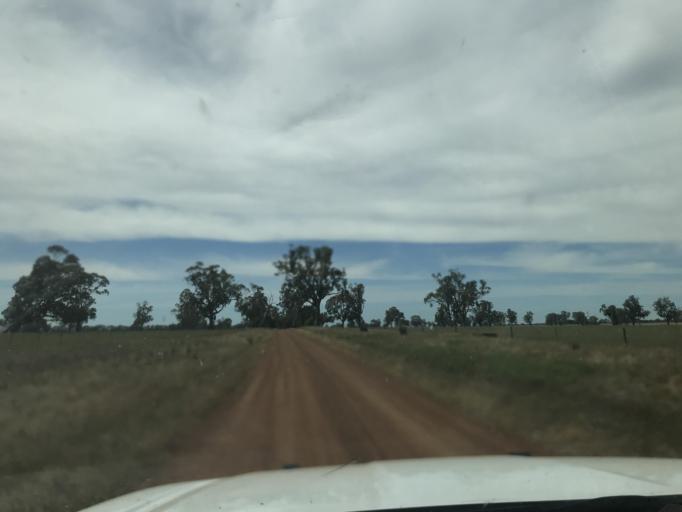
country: AU
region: South Australia
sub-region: Naracoorte and Lucindale
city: Naracoorte
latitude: -37.0054
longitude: 141.4662
